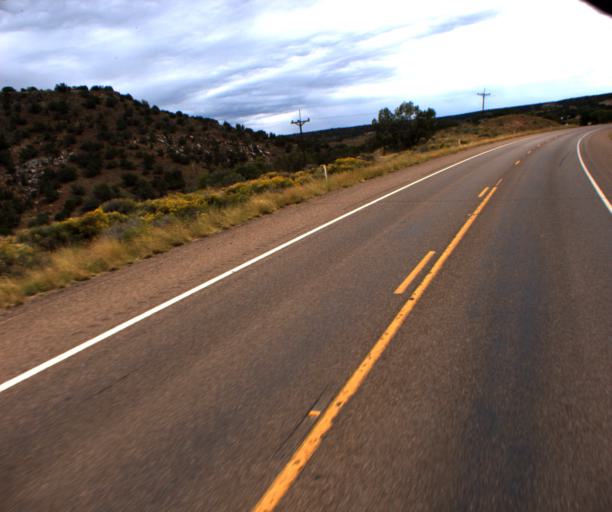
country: US
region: Arizona
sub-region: Navajo County
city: Taylor
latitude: 34.3950
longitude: -110.0660
